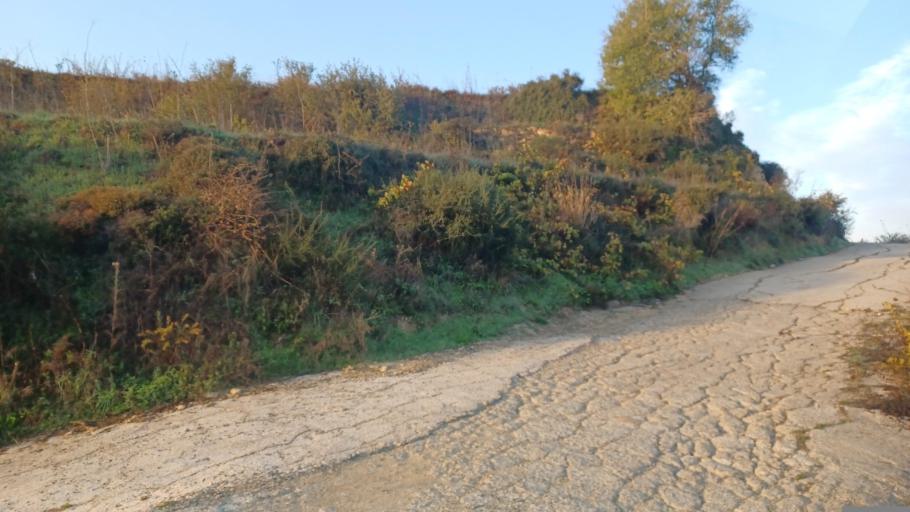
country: CY
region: Pafos
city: Mesogi
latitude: 34.8500
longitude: 32.4691
